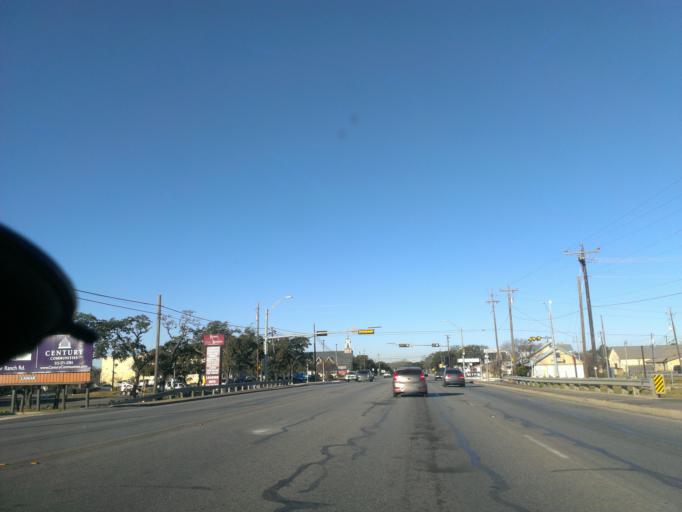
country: US
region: Texas
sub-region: Hays County
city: Dripping Springs
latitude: 30.1916
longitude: -98.0864
